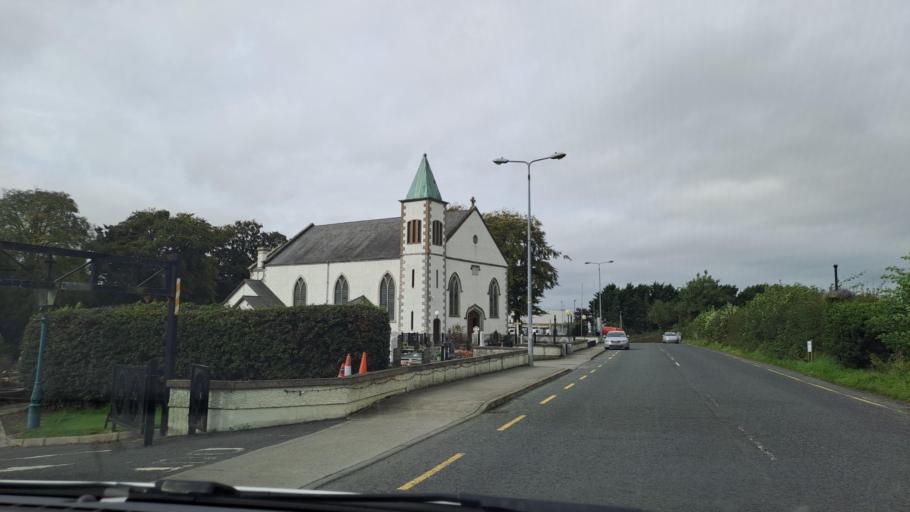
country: IE
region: Ulster
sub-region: An Cabhan
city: Bailieborough
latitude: 53.9962
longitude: -6.9003
